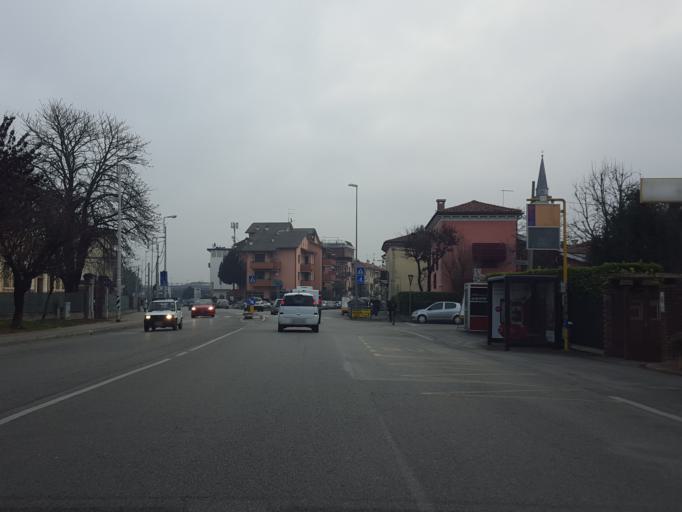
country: IT
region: Veneto
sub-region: Provincia di Vicenza
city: Vicenza
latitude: 45.5405
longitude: 11.5802
